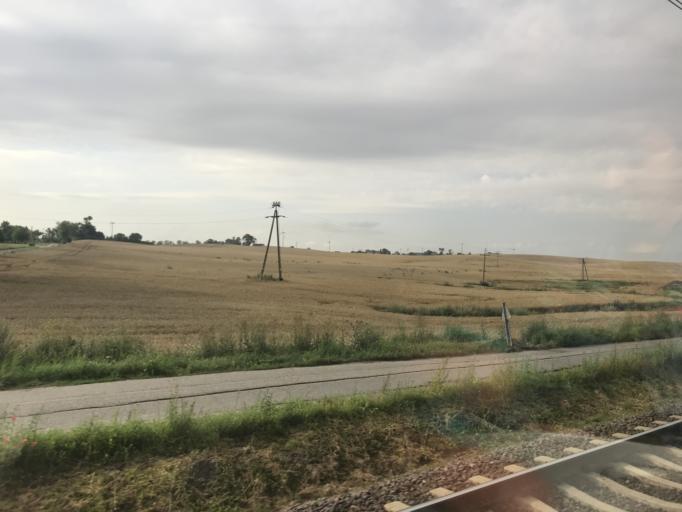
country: PL
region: Pomeranian Voivodeship
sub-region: Powiat tczewski
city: Pelplin
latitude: 53.9364
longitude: 18.7261
